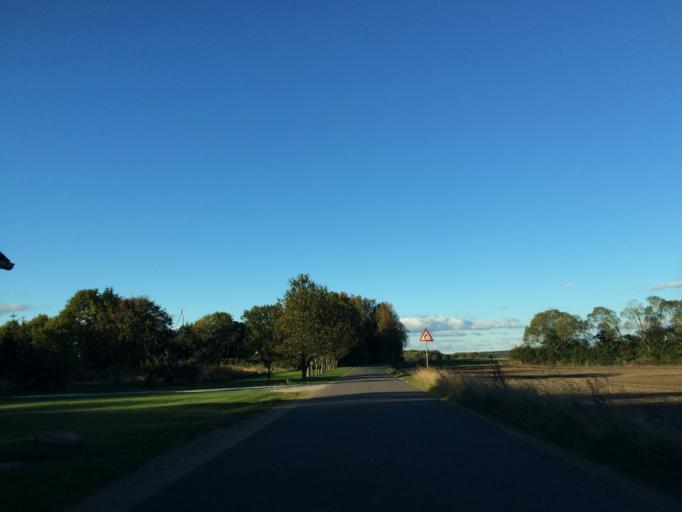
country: DK
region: Central Jutland
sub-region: Silkeborg Kommune
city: Svejbaek
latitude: 56.1689
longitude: 9.6931
